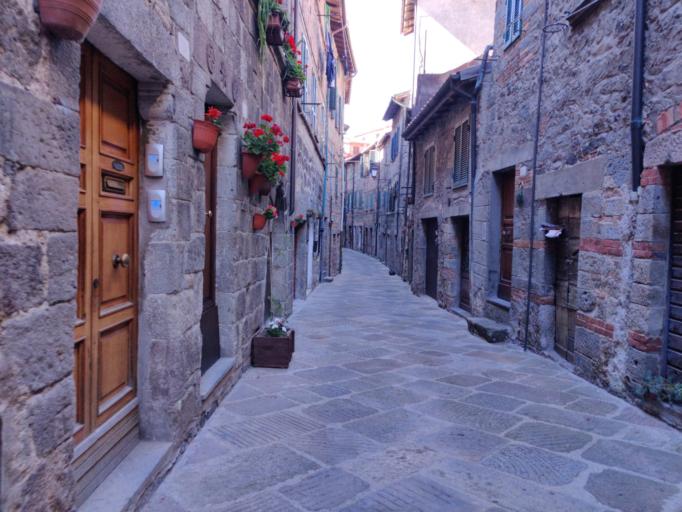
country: IT
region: Tuscany
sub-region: Provincia di Siena
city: Abbadia San Salvatore
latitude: 42.8809
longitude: 11.6782
